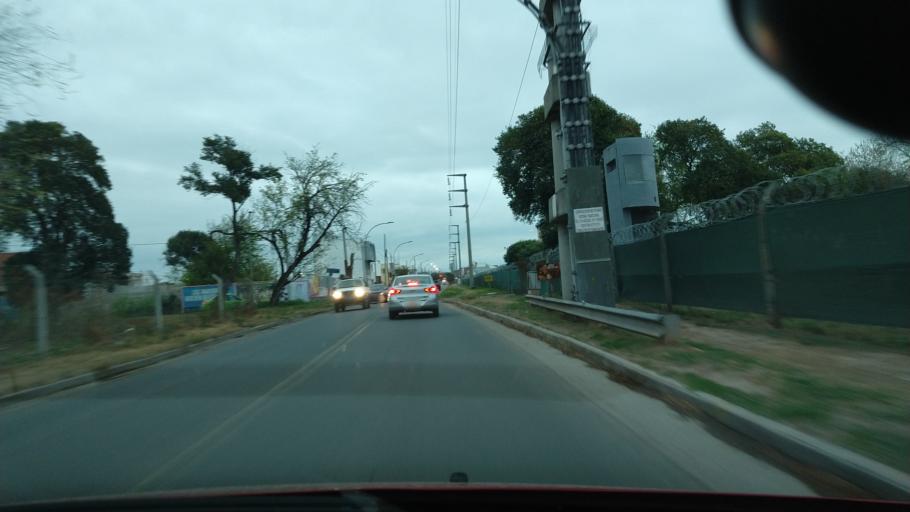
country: AR
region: Cordoba
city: La Calera
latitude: -31.3785
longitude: -64.2653
